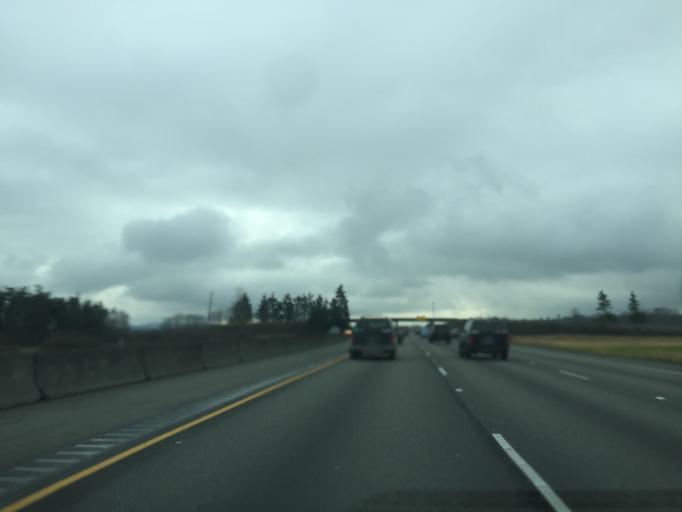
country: US
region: Washington
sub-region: Snohomish County
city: Marysville
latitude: 48.0105
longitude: -122.1746
